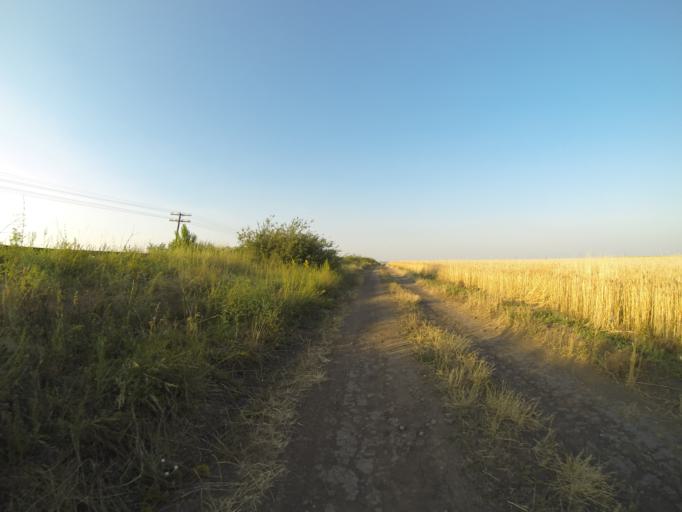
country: RO
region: Dolj
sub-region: Comuna Ceratu
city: Ceratu
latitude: 44.0546
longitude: 23.6762
